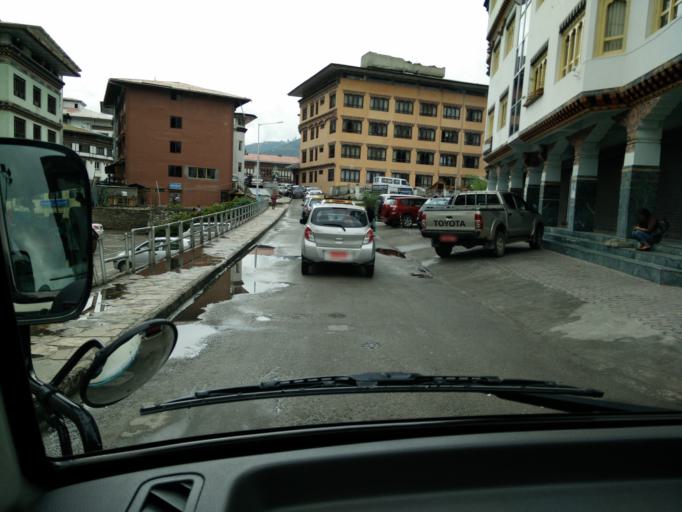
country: BT
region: Thimphu
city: Thimphu
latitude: 27.4723
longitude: 89.6378
